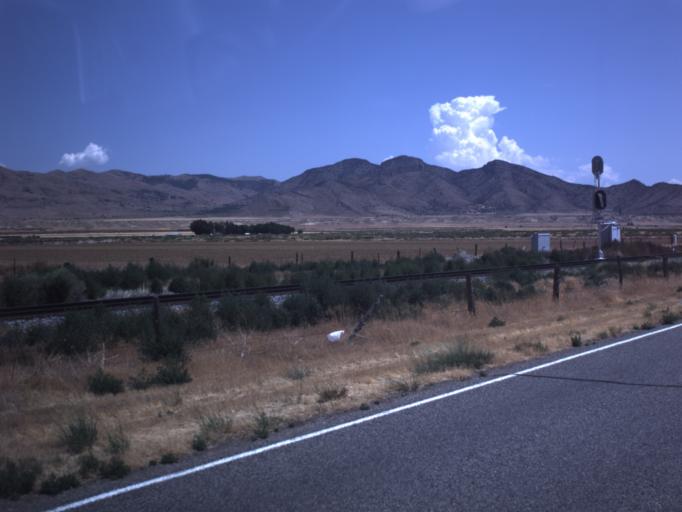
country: US
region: Utah
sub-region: Millard County
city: Delta
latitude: 39.5331
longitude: -112.3258
